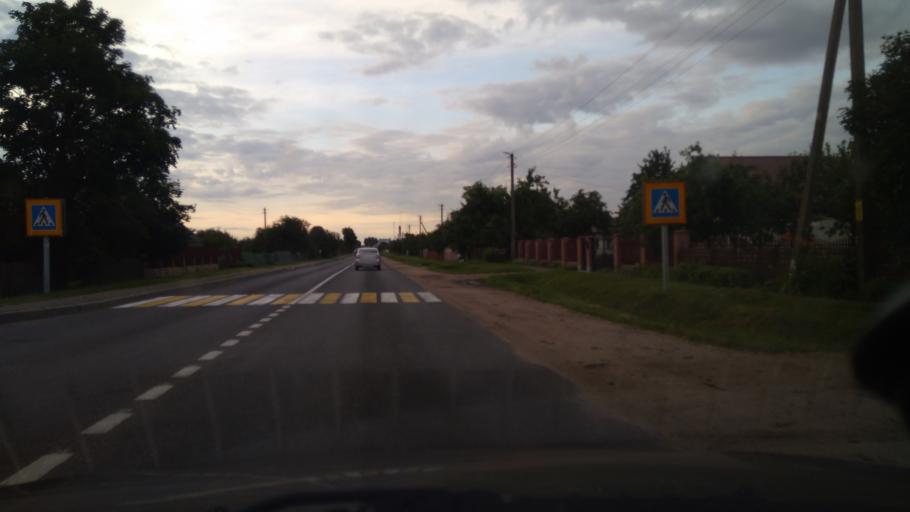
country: BY
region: Grodnenskaya
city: Shchuchin
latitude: 53.5833
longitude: 24.7476
